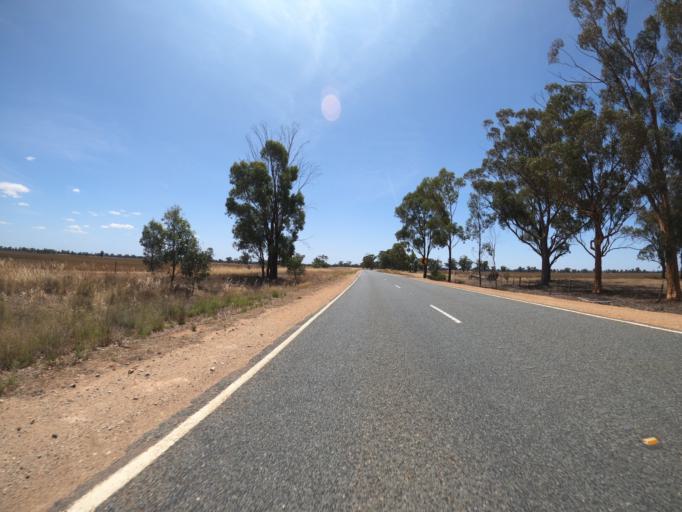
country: AU
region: Victoria
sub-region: Moira
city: Yarrawonga
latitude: -36.1980
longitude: 145.9672
